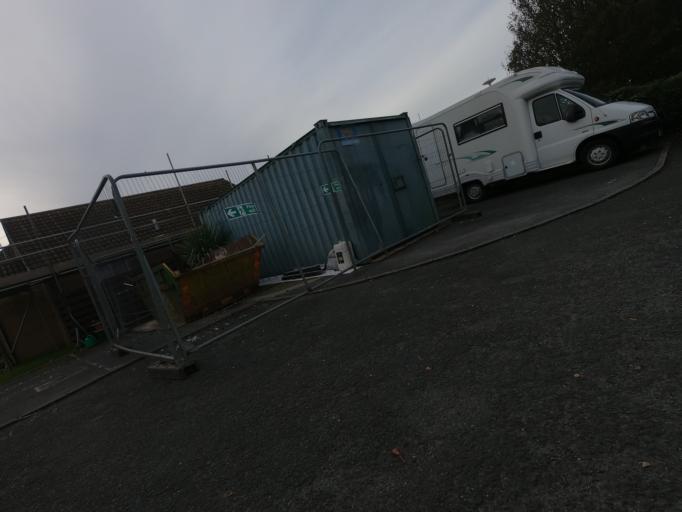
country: GB
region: England
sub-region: Borough of Torbay
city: Brixham
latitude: 50.3927
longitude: -3.5045
